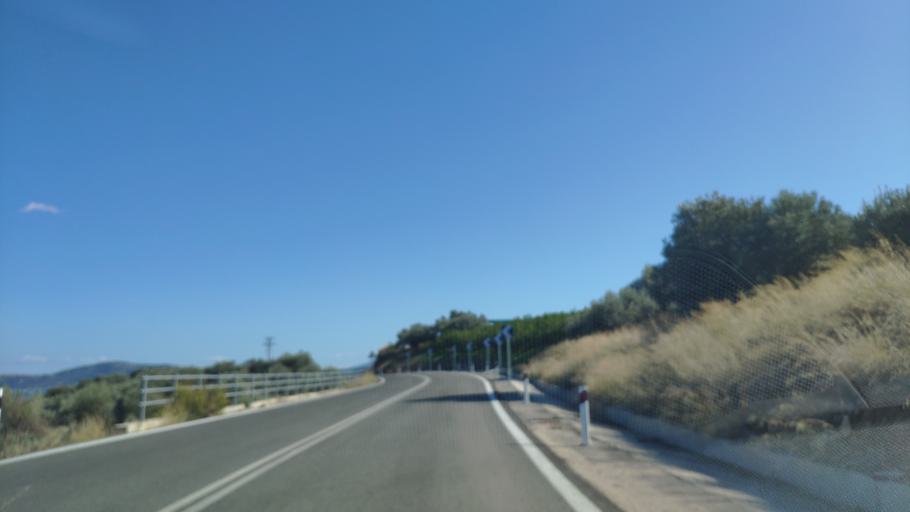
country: GR
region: Peloponnese
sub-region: Nomos Argolidos
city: Didyma
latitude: 37.5498
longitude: 23.2796
